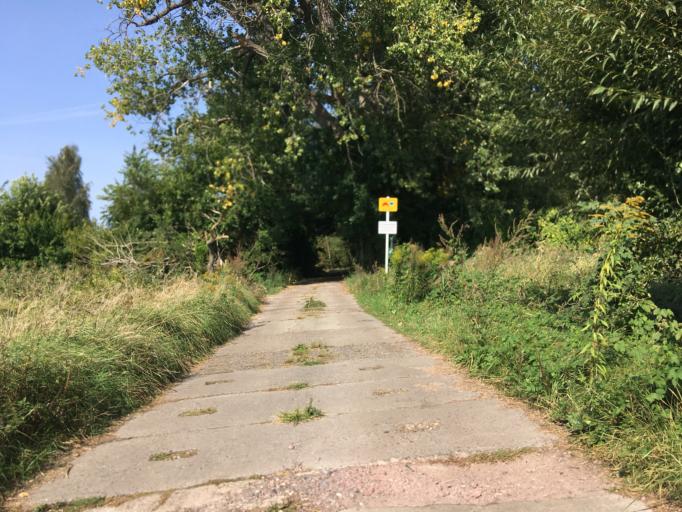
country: DE
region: Brandenburg
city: Erkner
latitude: 52.3997
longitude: 13.7311
